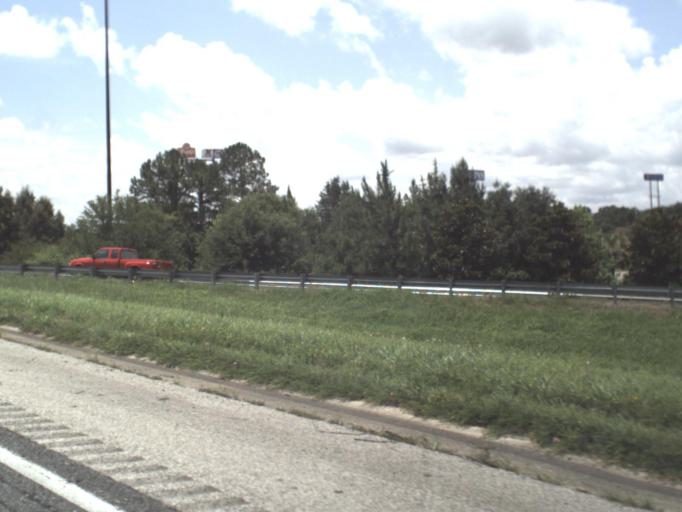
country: US
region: Florida
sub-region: Alachua County
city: High Springs
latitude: 29.8031
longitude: -82.5139
